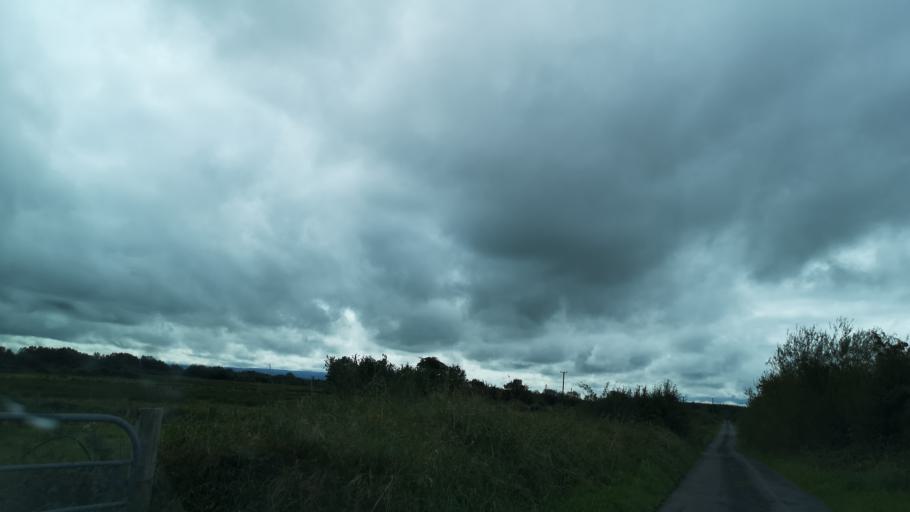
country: IE
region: Connaught
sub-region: County Galway
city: Loughrea
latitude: 53.3049
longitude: -8.5812
